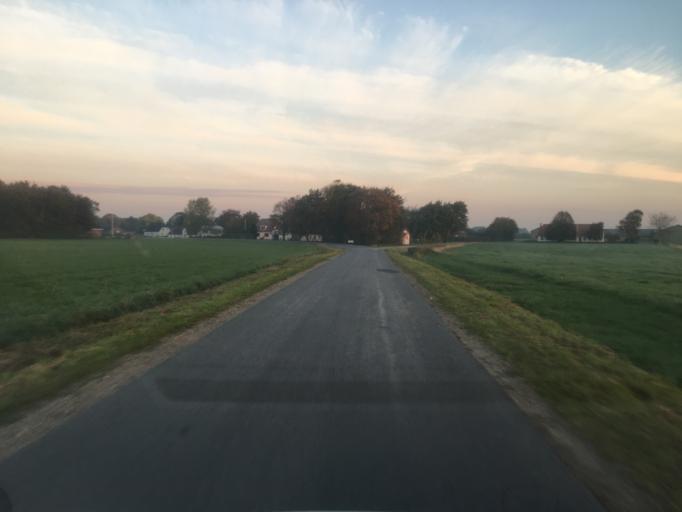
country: DK
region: South Denmark
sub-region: Tonder Kommune
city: Logumkloster
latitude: 54.9979
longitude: 9.0455
